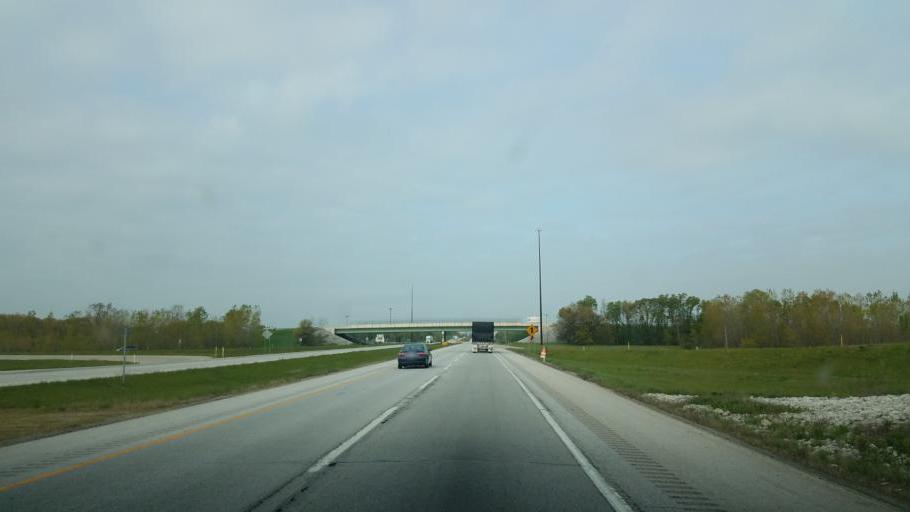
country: US
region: Indiana
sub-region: Elkhart County
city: Bristol
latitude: 41.7307
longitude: -85.8851
